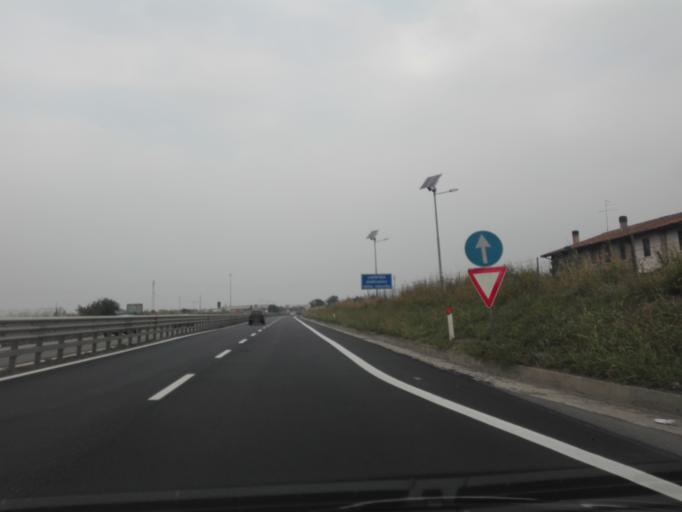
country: IT
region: Veneto
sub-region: Provincia di Verona
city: Campagnola
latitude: 45.3681
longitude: 11.0537
